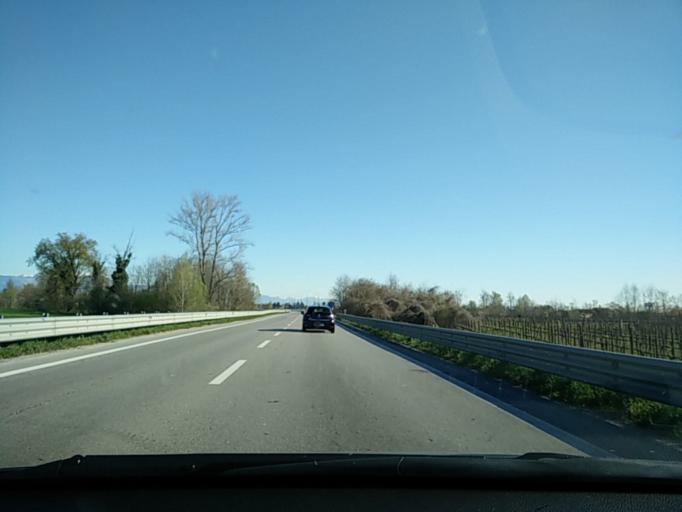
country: IT
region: Veneto
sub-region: Provincia di Treviso
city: Oderzo
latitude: 45.7766
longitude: 12.4735
